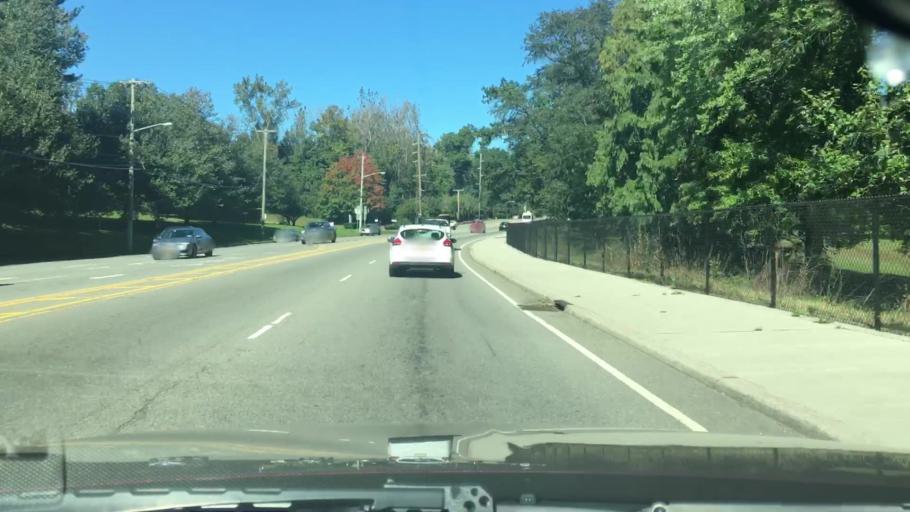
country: US
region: New York
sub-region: Nassau County
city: Searingtown
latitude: 40.7806
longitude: -73.6622
